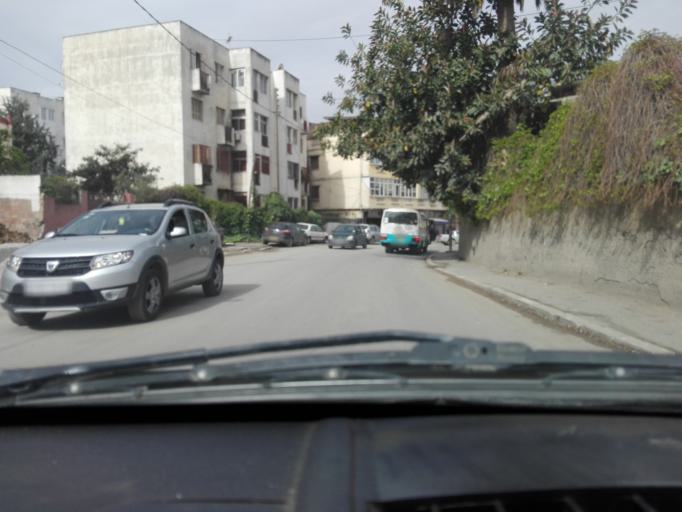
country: DZ
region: Alger
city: Bab Ezzouar
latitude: 36.7169
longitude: 3.1448
